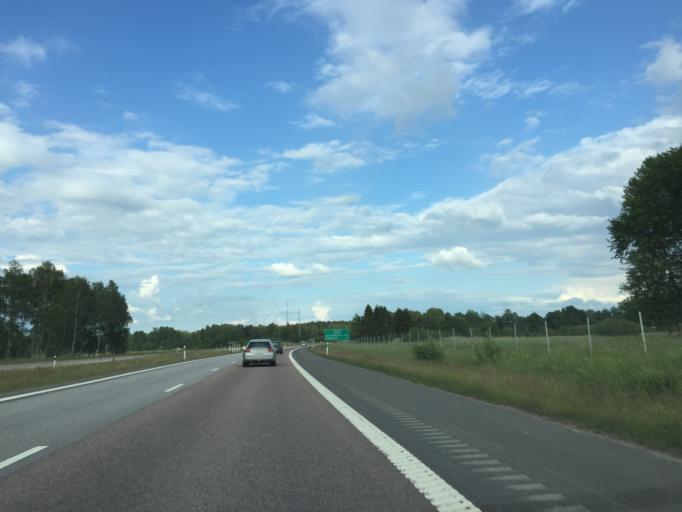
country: SE
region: OErebro
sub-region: Orebro Kommun
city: Hovsta
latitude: 59.3071
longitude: 15.2716
